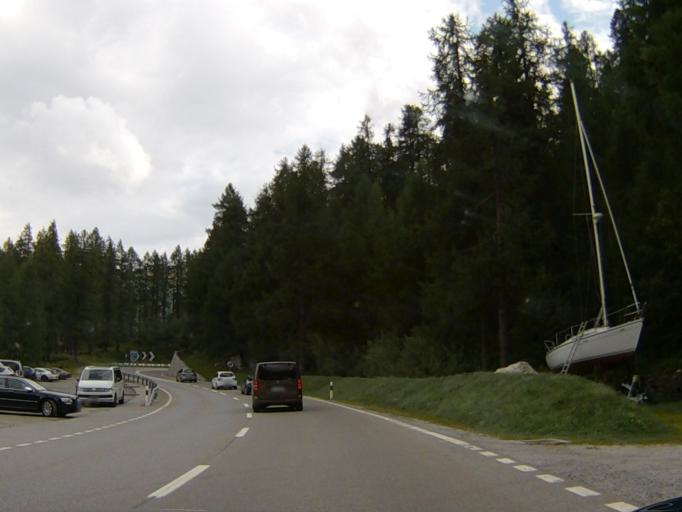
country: CH
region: Grisons
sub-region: Maloja District
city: Silvaplana
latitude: 46.4202
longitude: 9.7265
